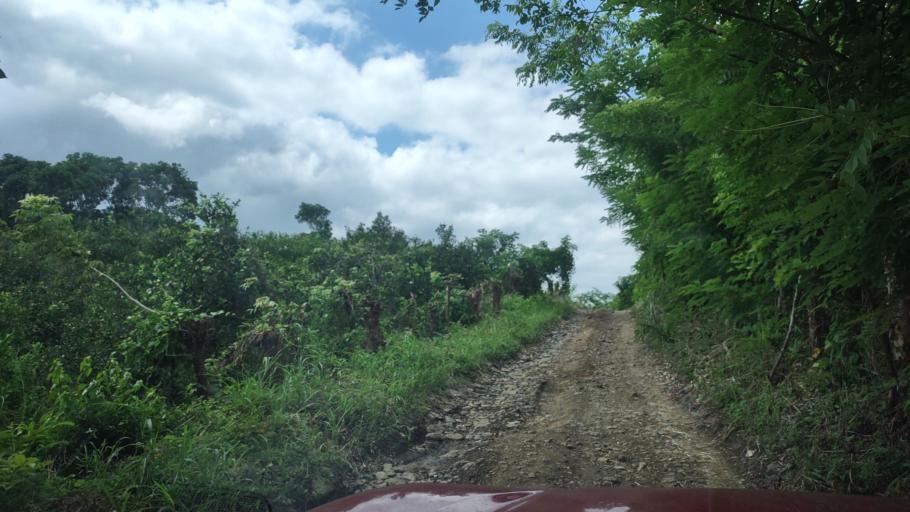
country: MX
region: Puebla
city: San Jose Acateno
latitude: 20.2241
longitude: -97.1565
